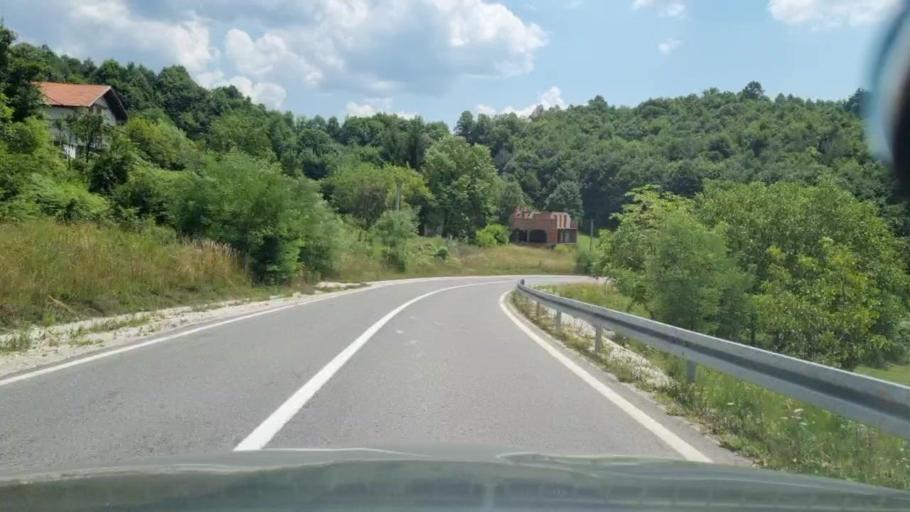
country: BA
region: Federation of Bosnia and Herzegovina
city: Tojsici
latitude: 44.5366
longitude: 18.8388
